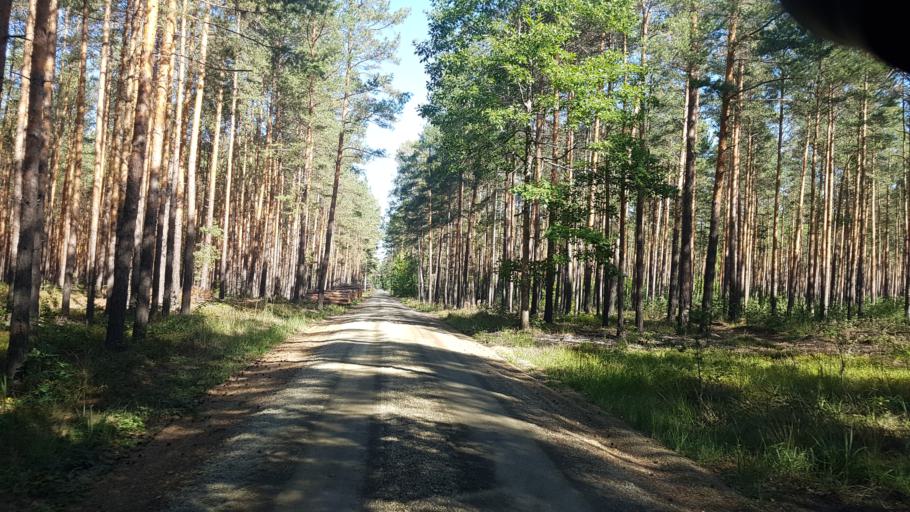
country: DE
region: Brandenburg
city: Hohenleipisch
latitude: 51.5337
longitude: 13.5821
